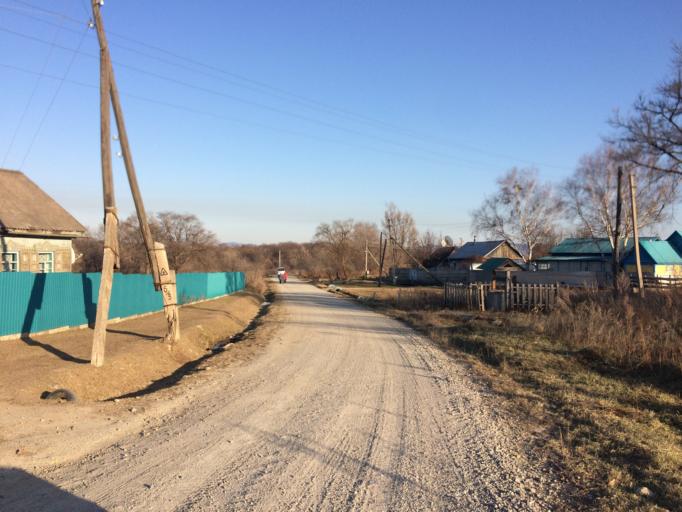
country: RU
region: Primorskiy
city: Ivanovka
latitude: 43.9572
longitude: 132.4757
